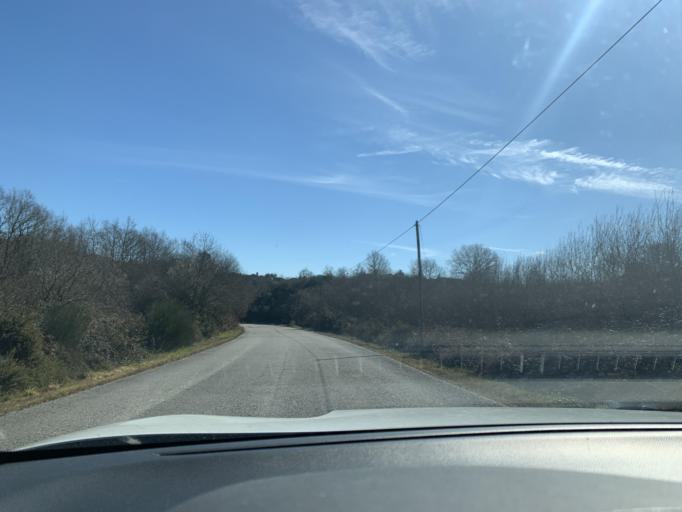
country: PT
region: Viseu
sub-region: Concelho de Tondela
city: Tondela
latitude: 40.5994
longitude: -8.0269
